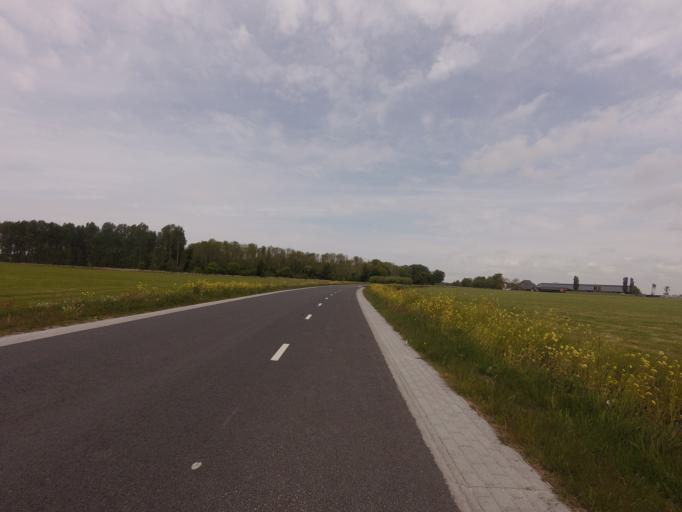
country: NL
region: Friesland
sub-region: Sudwest Fryslan
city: Bolsward
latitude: 53.0929
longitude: 5.4775
